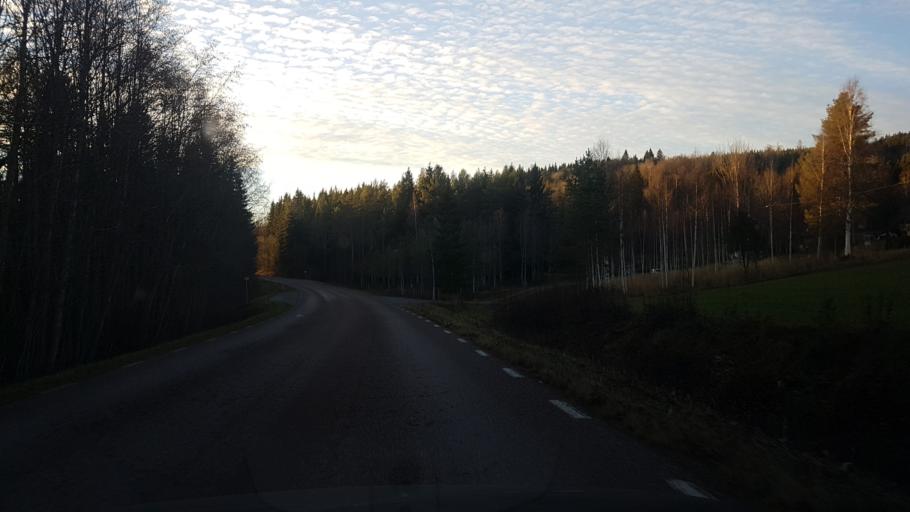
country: SE
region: Dalarna
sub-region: Leksand Municipality
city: Smedby
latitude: 60.7436
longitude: 15.1870
